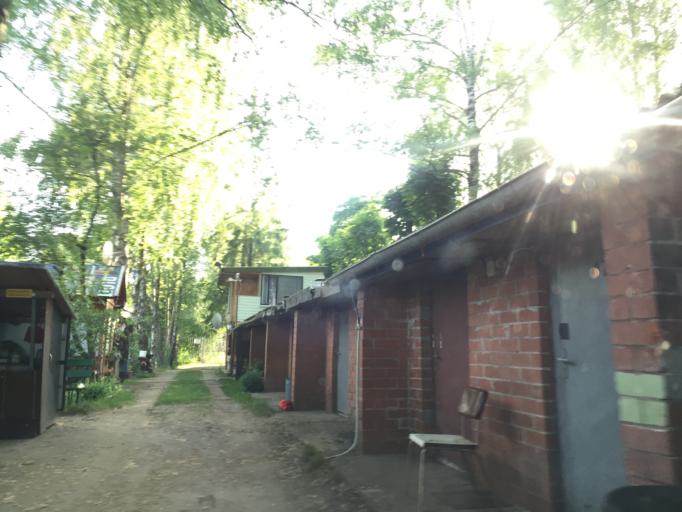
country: LV
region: Riga
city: Bergi
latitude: 56.9929
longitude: 24.2471
